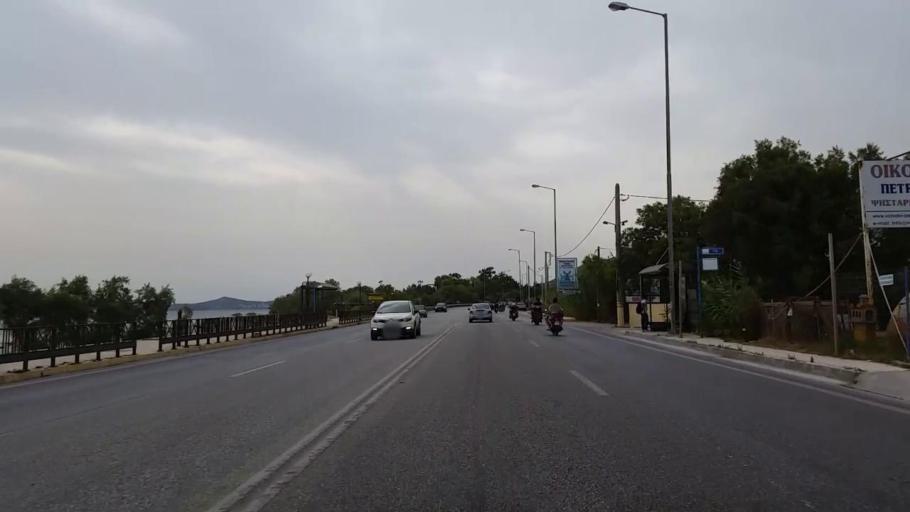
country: GR
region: Attica
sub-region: Nomarchia Anatolikis Attikis
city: Agios Dimitrios Kropias
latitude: 37.7892
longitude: 23.8830
